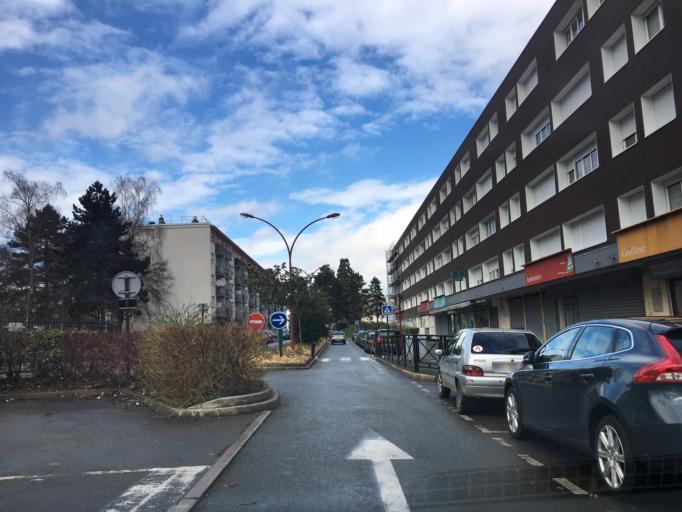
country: FR
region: Ile-de-France
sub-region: Departement du Val-d'Oise
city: Arnouville
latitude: 49.0028
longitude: 2.4234
